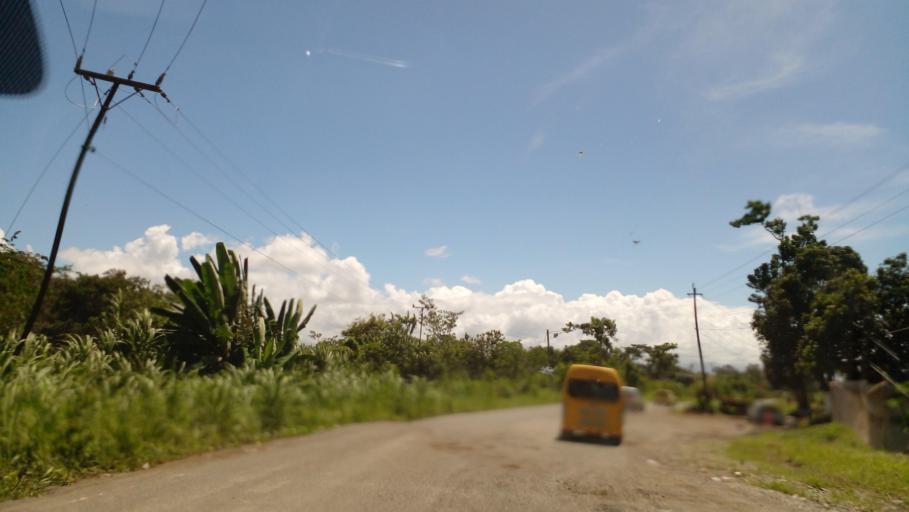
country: PA
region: Bocas del Toro
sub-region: Distrito de Changuinola
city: Changuinola
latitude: 9.4656
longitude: -82.5515
